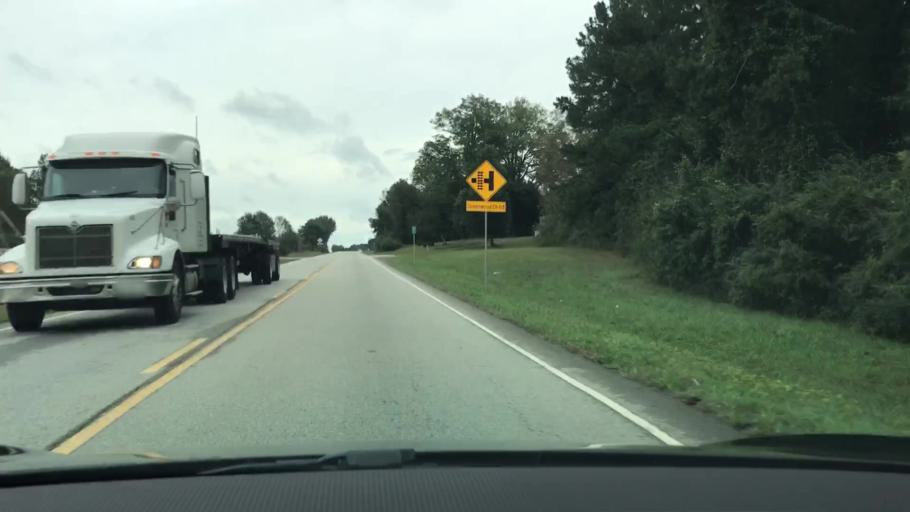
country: US
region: Georgia
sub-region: Taliaferro County
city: Crawfordville
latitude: 33.4950
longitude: -82.8014
